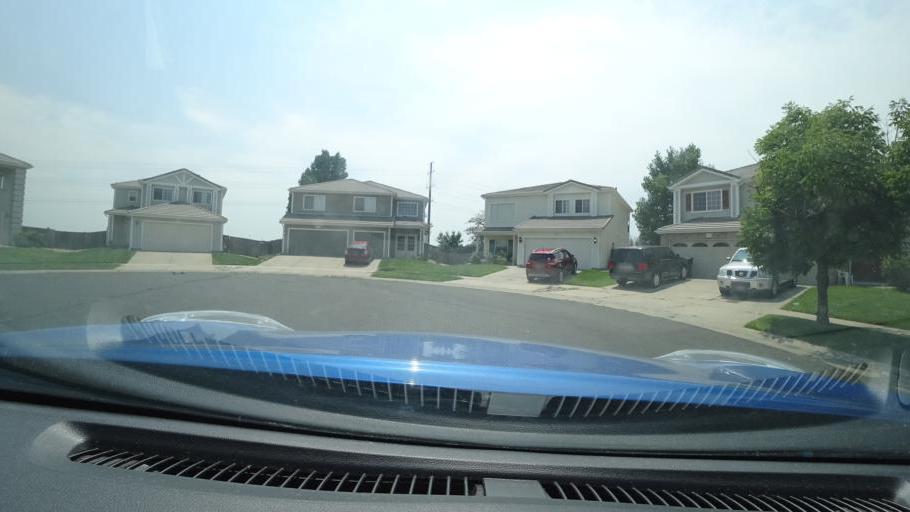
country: US
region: Colorado
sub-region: Adams County
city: Aurora
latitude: 39.7705
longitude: -104.7507
